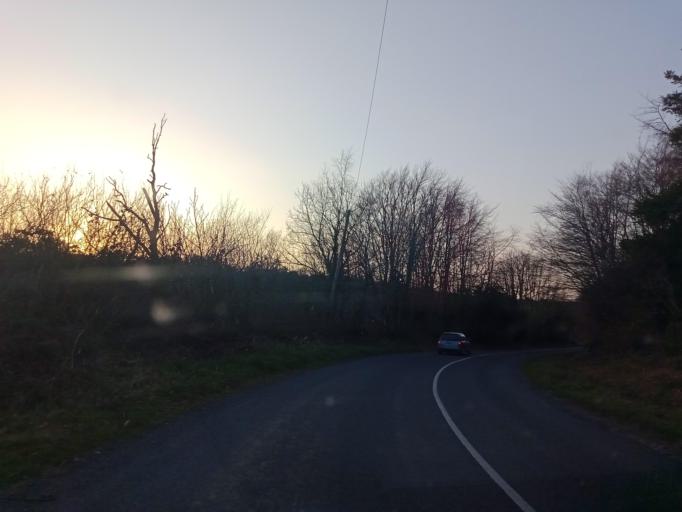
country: IE
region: Leinster
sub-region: Kilkenny
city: Castlecomer
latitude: 52.8404
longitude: -7.2563
